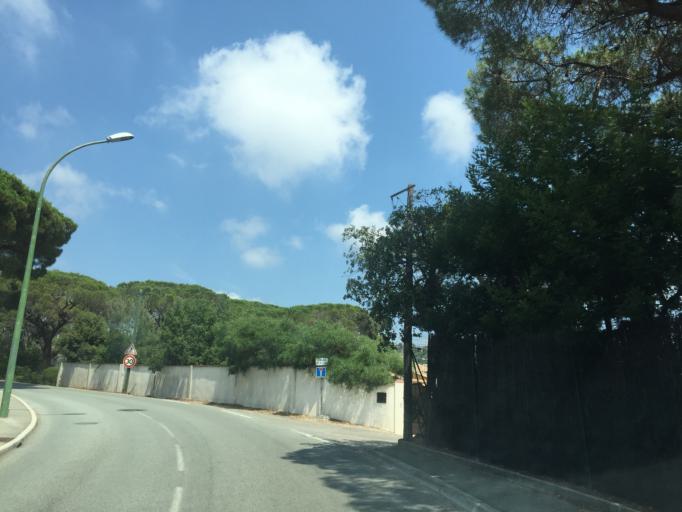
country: FR
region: Provence-Alpes-Cote d'Azur
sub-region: Departement du Var
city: Sainte-Maxime
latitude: 43.3451
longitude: 6.6777
